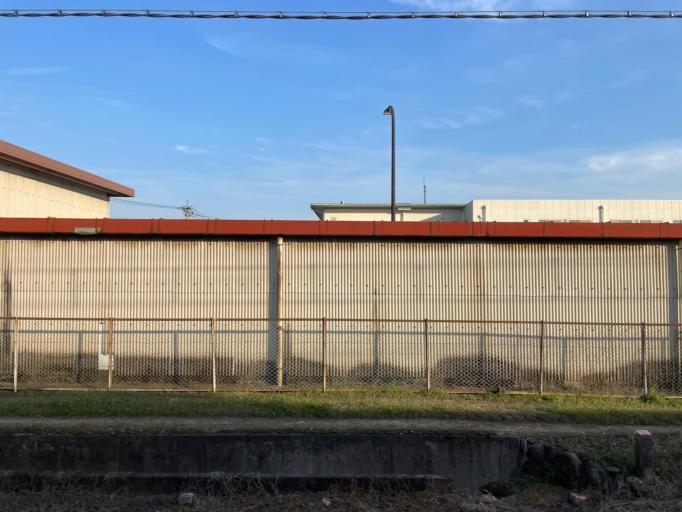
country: JP
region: Gunma
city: Annaka
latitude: 36.3245
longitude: 138.9014
